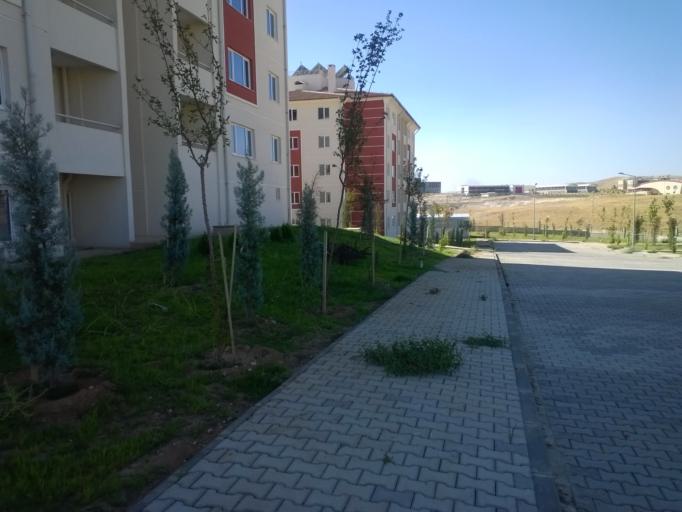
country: TR
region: Batman
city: Oymatas
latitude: 37.7844
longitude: 41.0713
